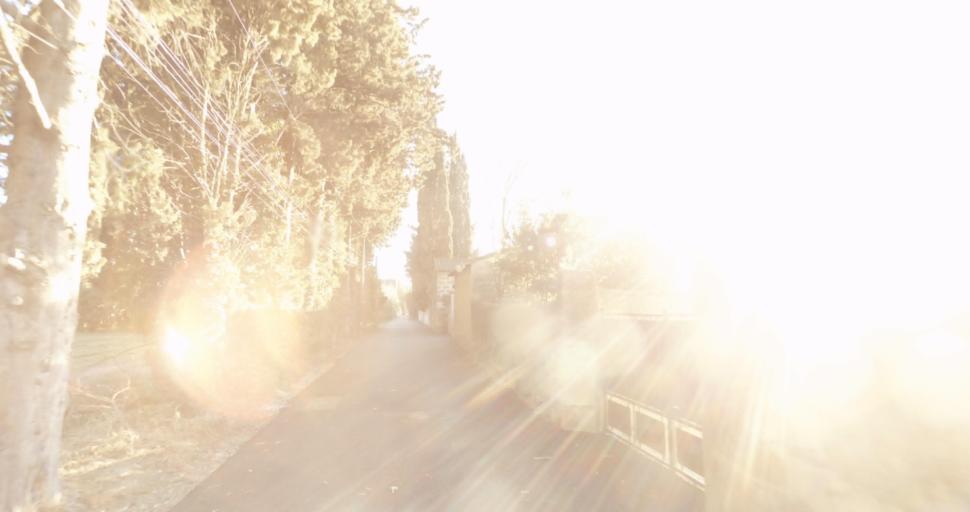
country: FR
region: Provence-Alpes-Cote d'Azur
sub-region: Departement des Bouches-du-Rhone
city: Barbentane
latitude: 43.9043
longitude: 4.7440
